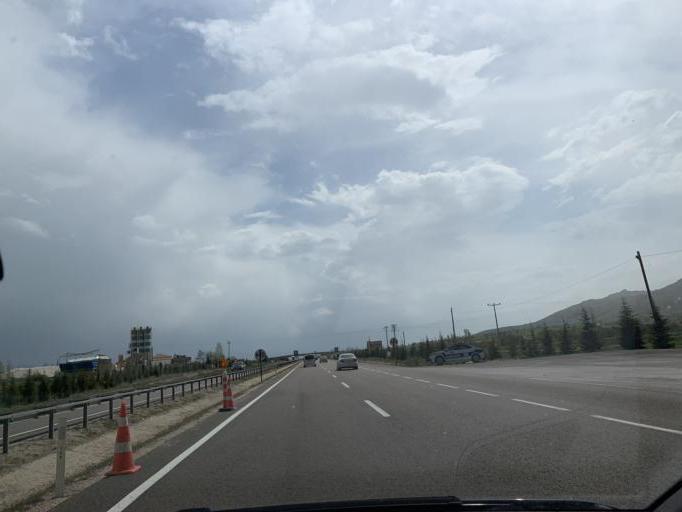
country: TR
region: Eskisehir
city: Sivrihisar
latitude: 39.4591
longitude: 31.5768
